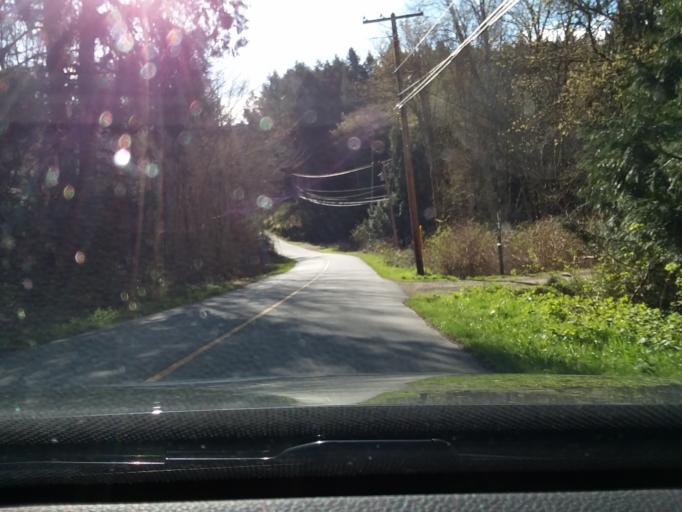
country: CA
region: British Columbia
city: North Cowichan
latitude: 48.9427
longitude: -123.5009
